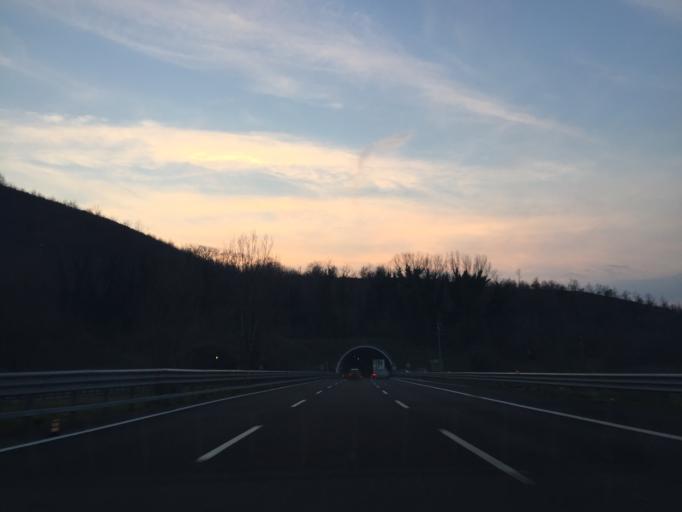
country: IT
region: Campania
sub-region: Provincia di Salerno
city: Mercato San Severino
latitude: 40.7704
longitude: 14.7450
